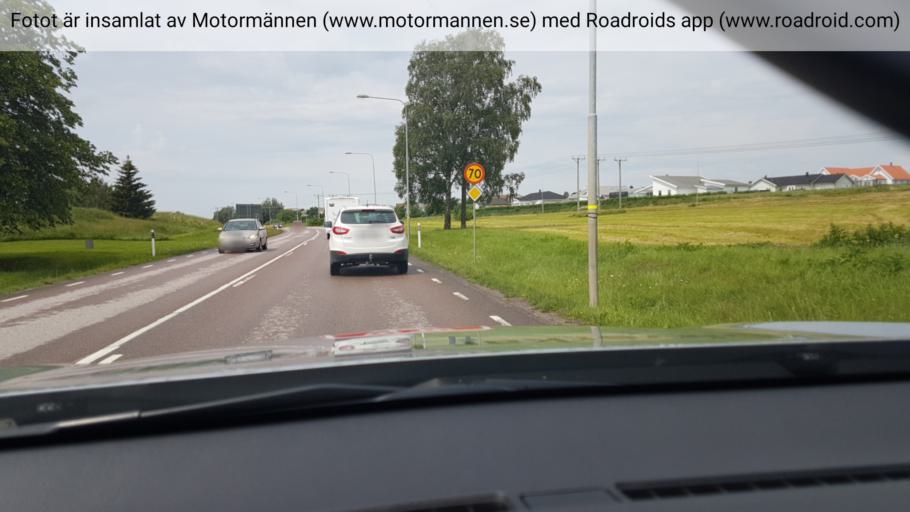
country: SE
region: Vaestra Goetaland
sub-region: Skara Kommun
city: Skara
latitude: 58.3929
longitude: 13.4607
